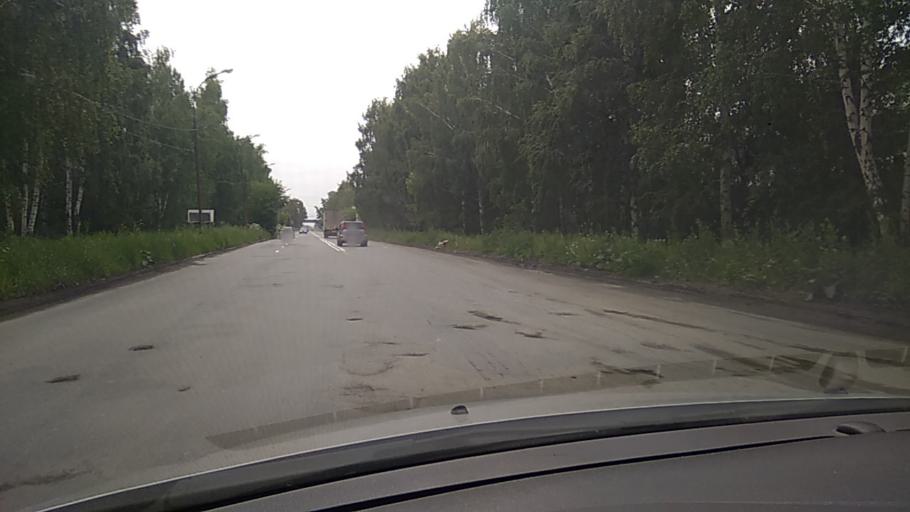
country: RU
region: Sverdlovsk
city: Shuvakish
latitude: 56.8915
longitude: 60.5177
